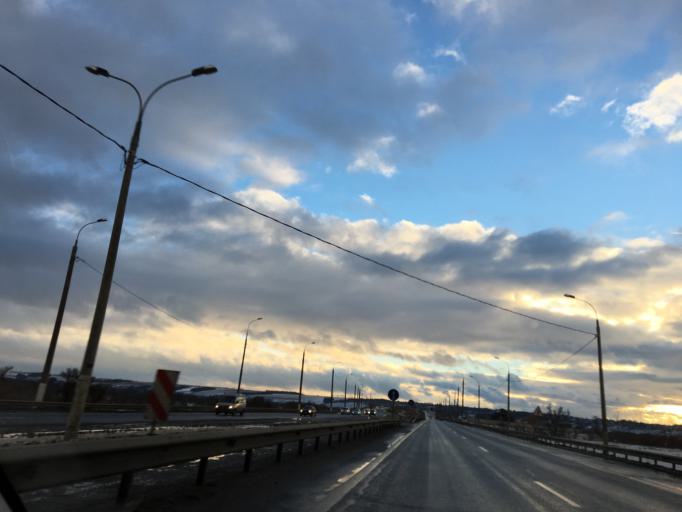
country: RU
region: Moskovskaya
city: Danki
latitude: 54.8763
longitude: 37.5073
